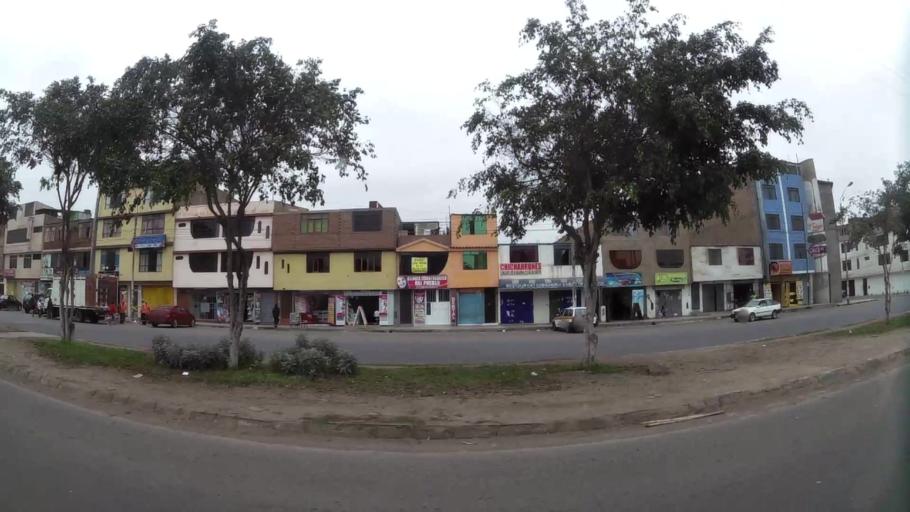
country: PE
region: Lima
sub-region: Lima
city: Independencia
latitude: -11.9783
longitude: -77.0840
